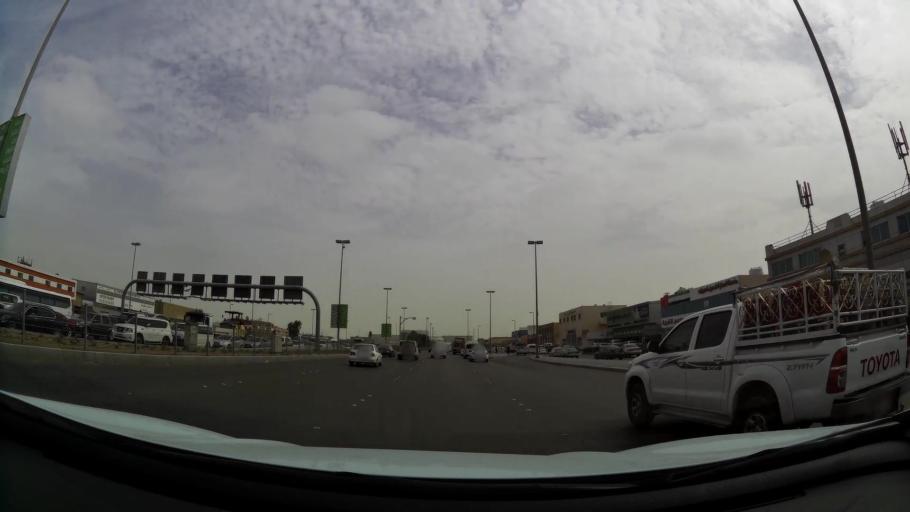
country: AE
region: Abu Dhabi
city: Abu Dhabi
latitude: 24.3731
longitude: 54.5125
